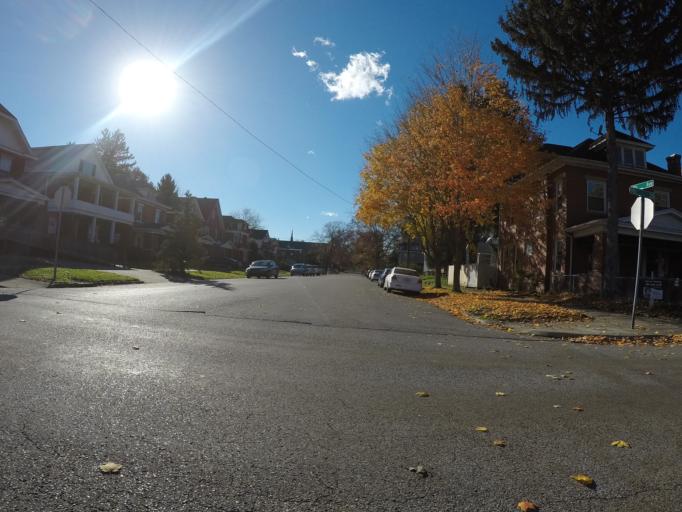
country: US
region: West Virginia
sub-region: Cabell County
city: Huntington
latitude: 38.4097
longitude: -82.4408
